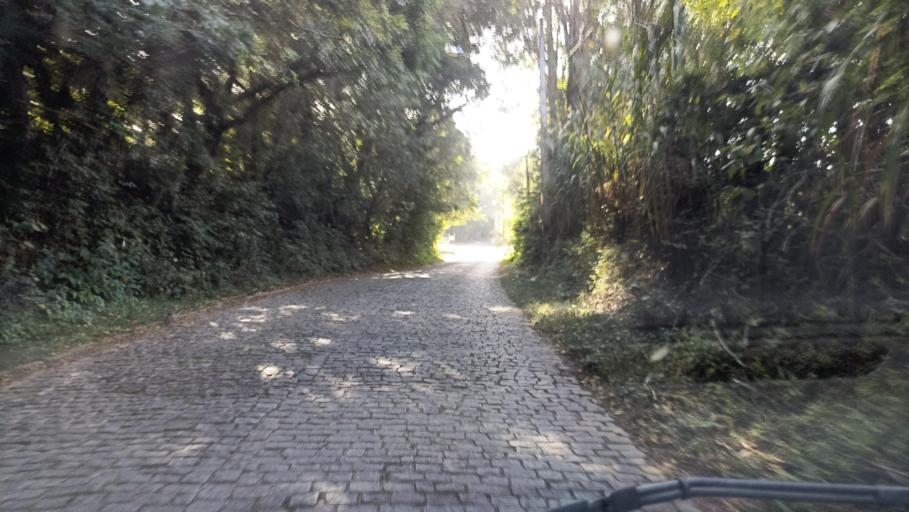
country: BR
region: Minas Gerais
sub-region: Tiradentes
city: Tiradentes
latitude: -21.1198
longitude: -44.1952
